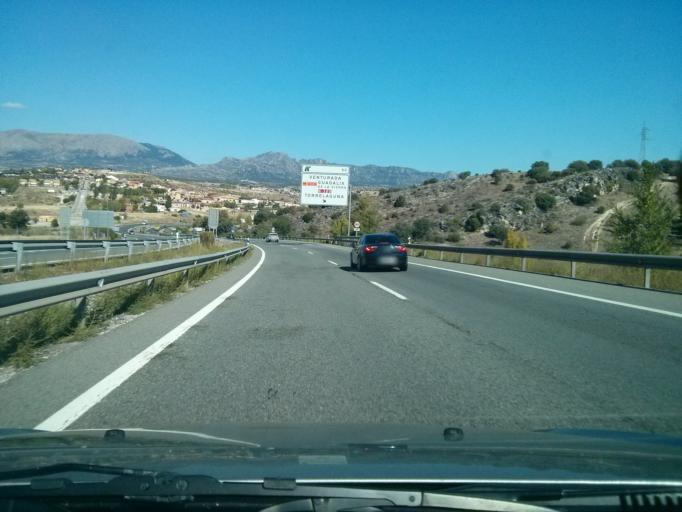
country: ES
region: Madrid
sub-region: Provincia de Madrid
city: Venturada
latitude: 40.7888
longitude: -3.6158
